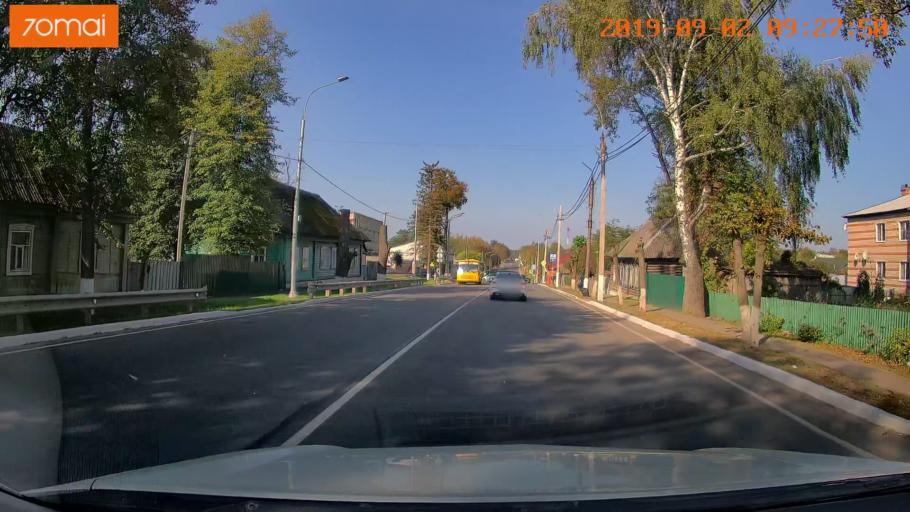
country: RU
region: Kaluga
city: Yukhnov
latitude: 54.7440
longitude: 35.2376
